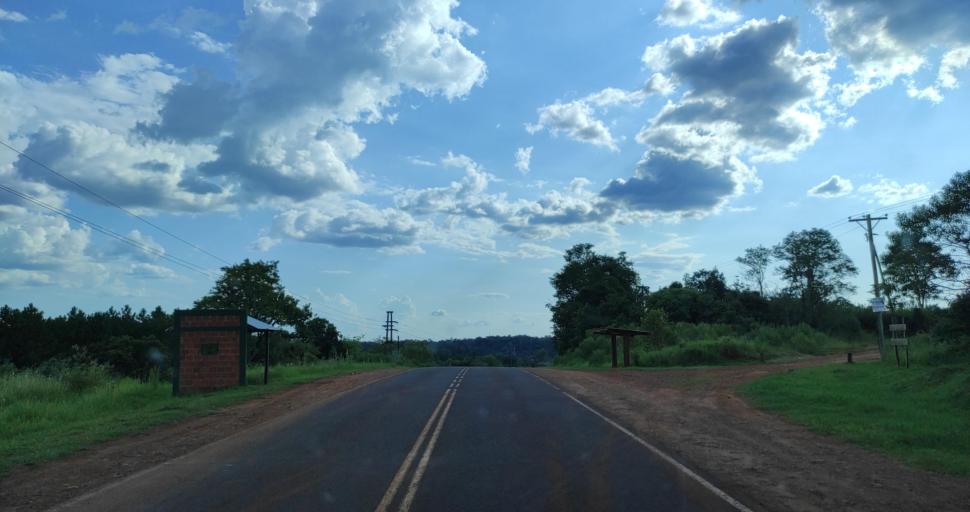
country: AR
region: Misiones
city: San Vicente
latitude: -26.3389
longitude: -54.1778
